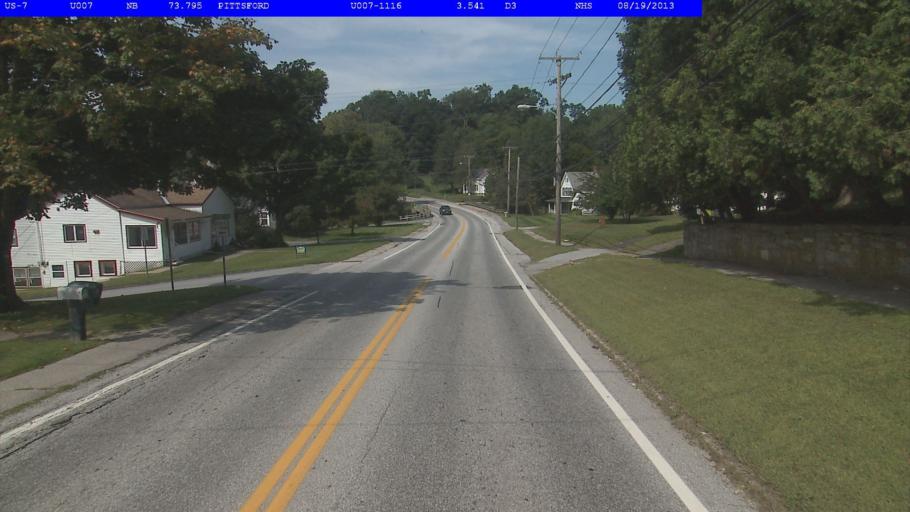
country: US
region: Vermont
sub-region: Rutland County
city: Rutland
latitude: 43.7067
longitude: -73.0196
